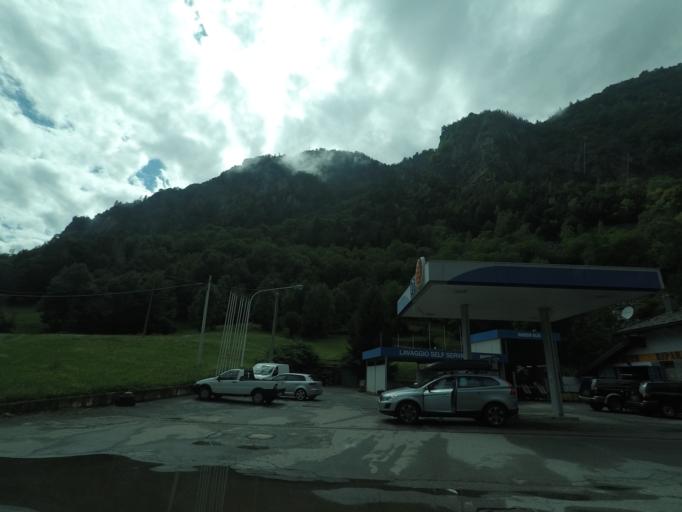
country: IT
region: Aosta Valley
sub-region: Valle d'Aosta
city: Antey-Saint-Andre
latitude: 45.8131
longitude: 7.5885
